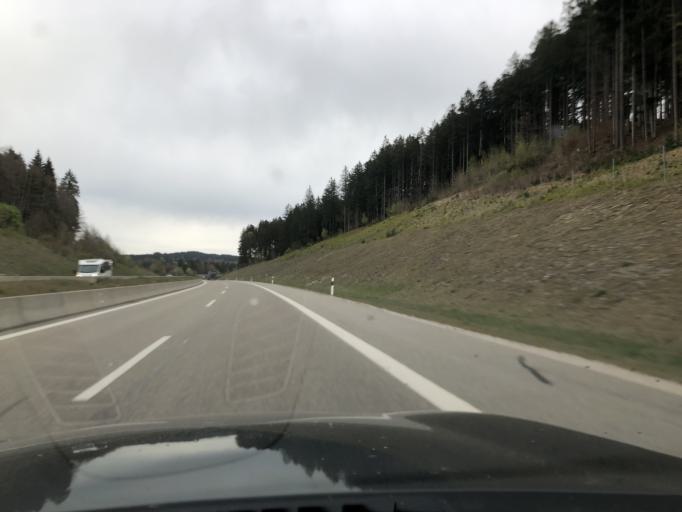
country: DE
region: Bavaria
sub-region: Swabia
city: Hopferau
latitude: 47.6261
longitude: 10.6402
